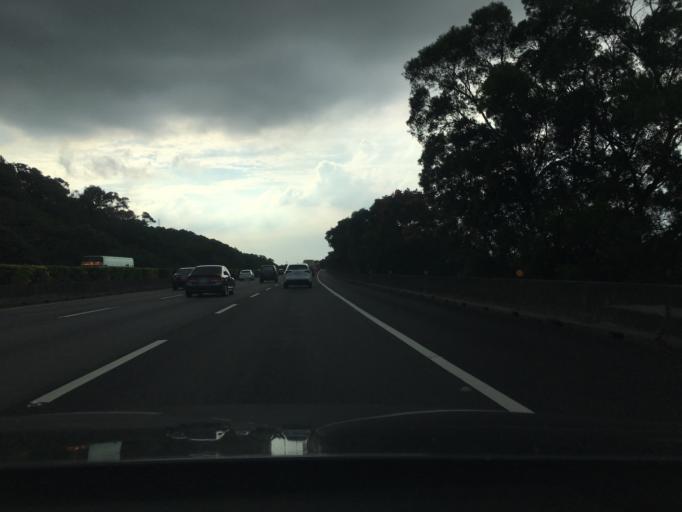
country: TW
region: Taiwan
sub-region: Hsinchu
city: Zhubei
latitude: 24.8850
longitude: 121.0865
